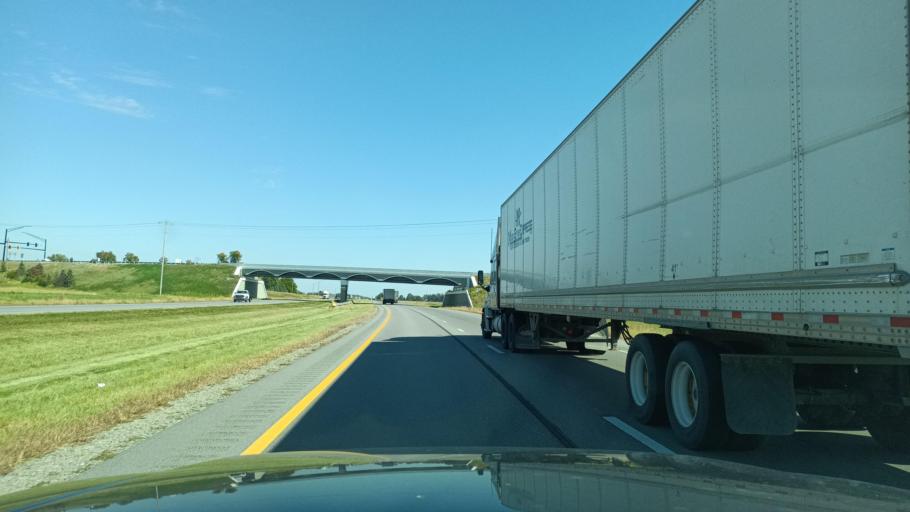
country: US
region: Ohio
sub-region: Defiance County
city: Defiance
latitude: 41.3106
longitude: -84.3254
